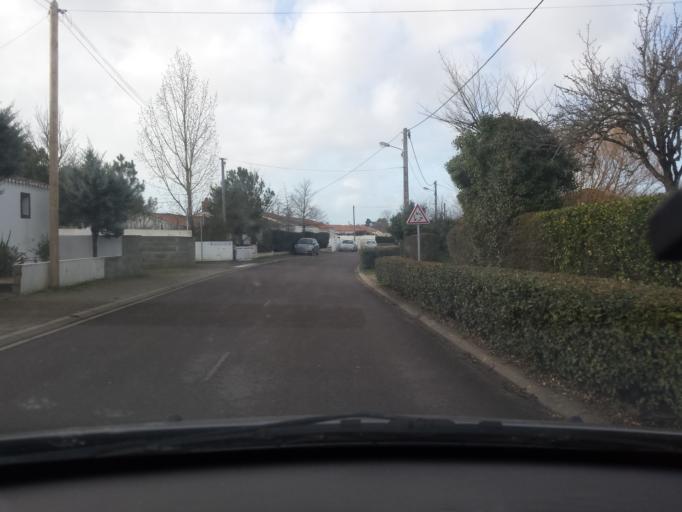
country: FR
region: Pays de la Loire
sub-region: Departement de la Vendee
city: Olonne-sur-Mer
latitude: 46.5634
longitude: -1.7751
